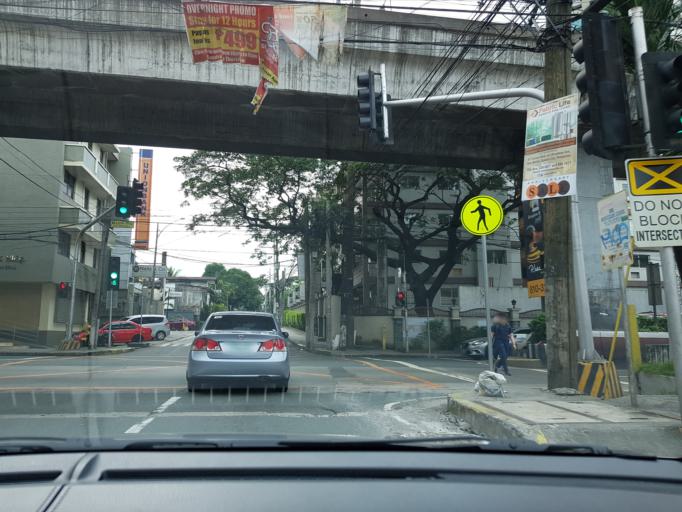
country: PH
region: Metro Manila
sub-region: San Juan
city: San Juan
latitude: 14.6169
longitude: 121.0396
